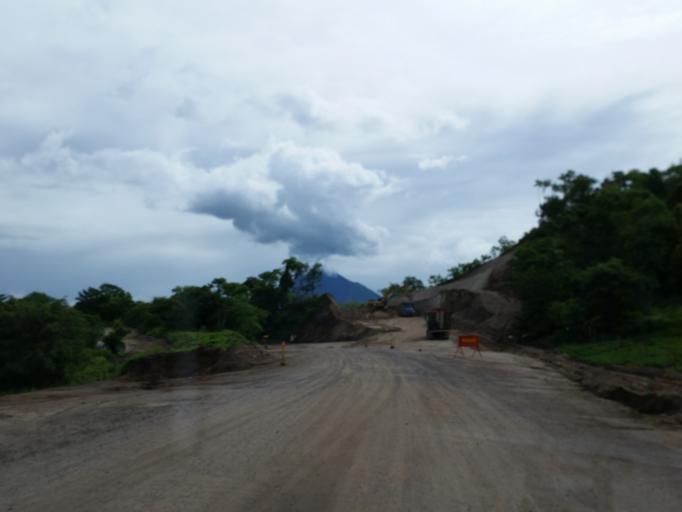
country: NI
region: Leon
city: La Paz Centro
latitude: 12.4050
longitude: -86.6495
